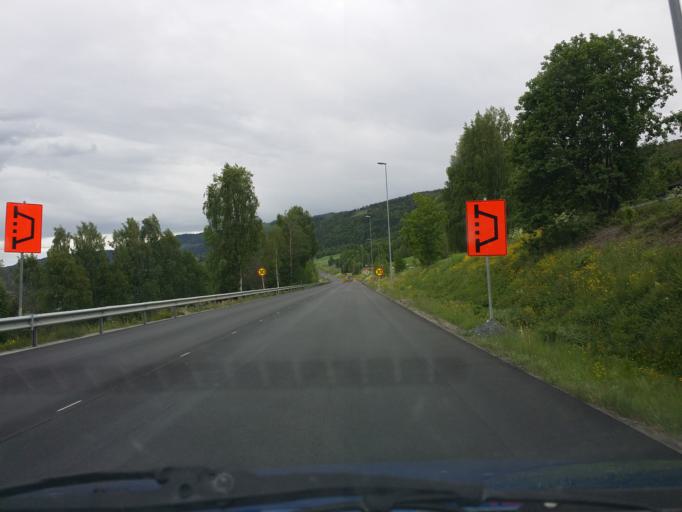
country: NO
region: Oppland
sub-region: Lillehammer
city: Lillehammer
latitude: 61.0376
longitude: 10.4402
